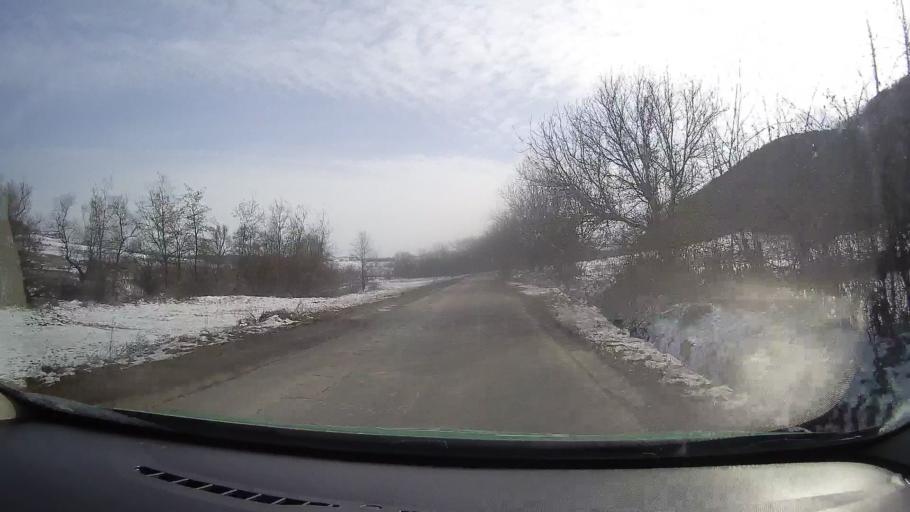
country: RO
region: Mures
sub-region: Comuna Apold
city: Saes
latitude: 46.1940
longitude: 24.7646
